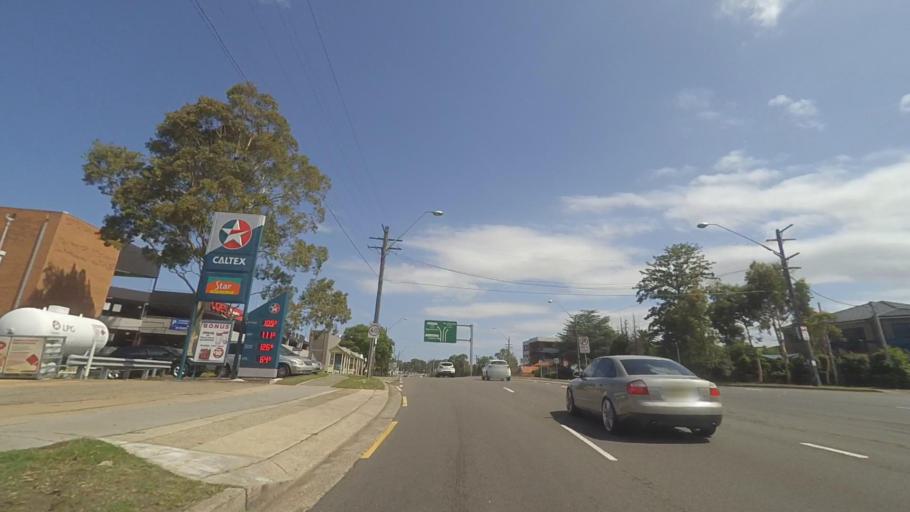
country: AU
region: New South Wales
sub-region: Parramatta
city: Carlingford
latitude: -33.7759
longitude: 151.0515
